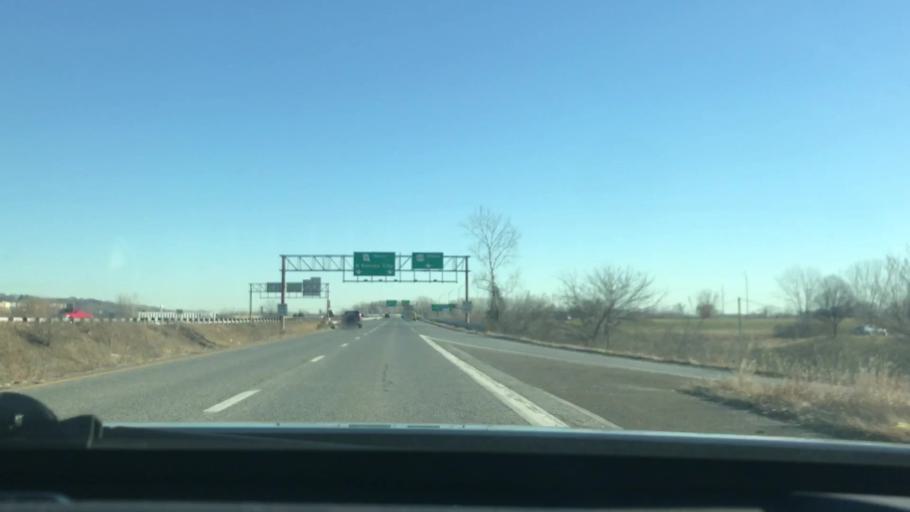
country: US
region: Missouri
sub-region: Platte County
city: Riverside
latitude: 39.1699
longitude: -94.6198
